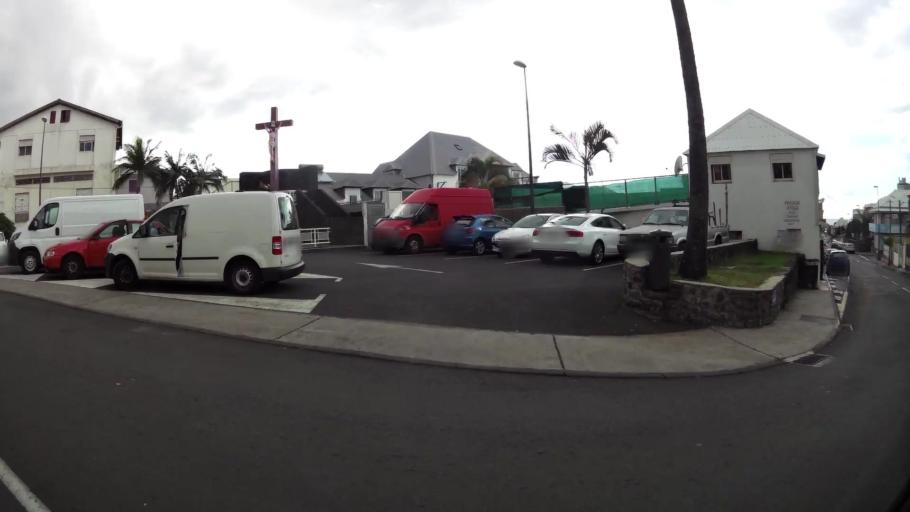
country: RE
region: Reunion
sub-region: Reunion
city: Saint-Denis
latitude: -20.8836
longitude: 55.4587
